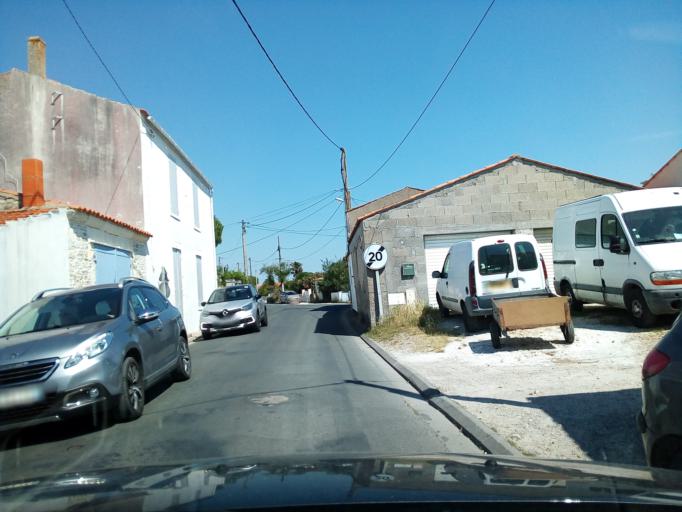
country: FR
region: Poitou-Charentes
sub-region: Departement de la Charente-Maritime
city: Boyard-Ville
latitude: 45.9710
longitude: -1.2939
